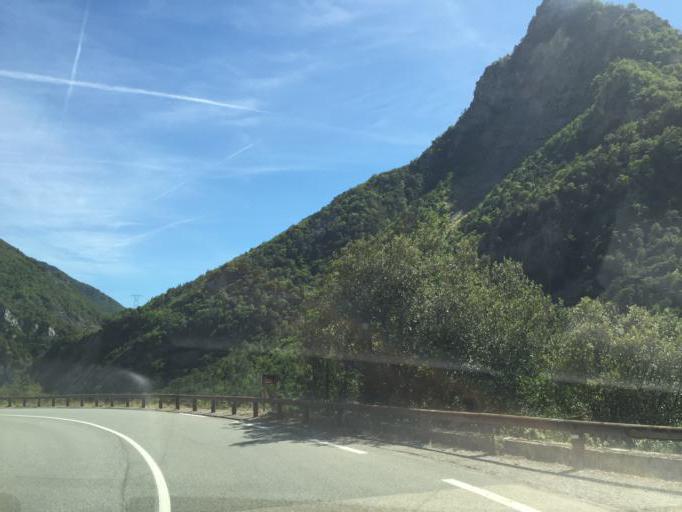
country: FR
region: Provence-Alpes-Cote d'Azur
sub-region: Departement des Alpes-Maritimes
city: Saint-Martin-Vesubie
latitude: 44.0529
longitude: 7.1244
